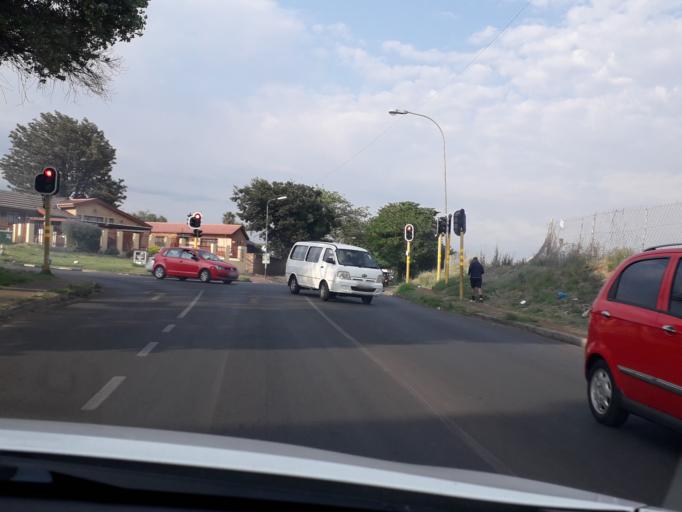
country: ZA
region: Gauteng
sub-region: City of Johannesburg Metropolitan Municipality
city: Johannesburg
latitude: -26.1708
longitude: 27.9733
